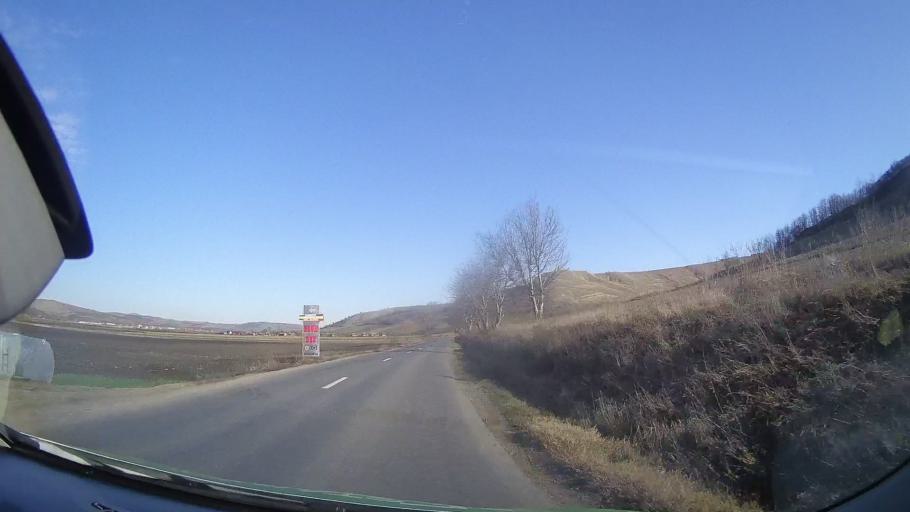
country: RO
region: Mures
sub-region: Comuna Iclanzel
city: Iclanzel
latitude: 46.5505
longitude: 24.3293
